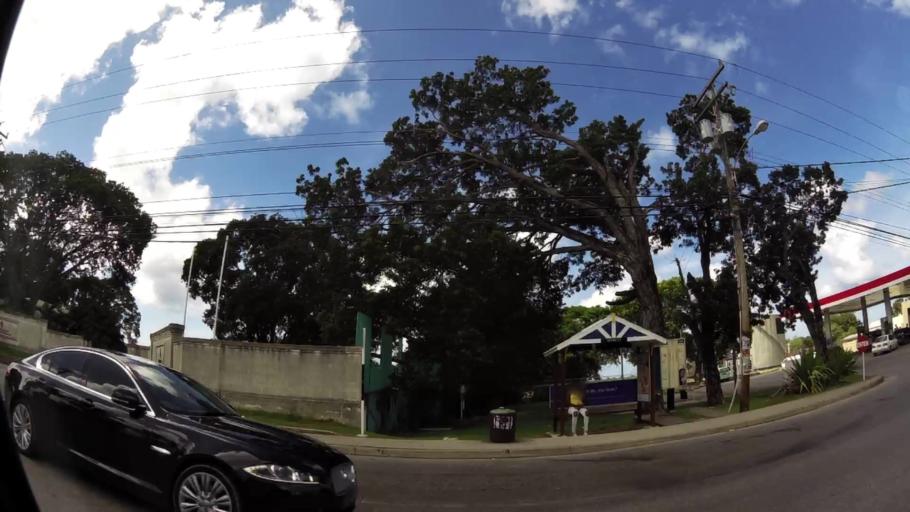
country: BB
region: Saint Michael
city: Bridgetown
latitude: 13.1327
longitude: -59.6330
